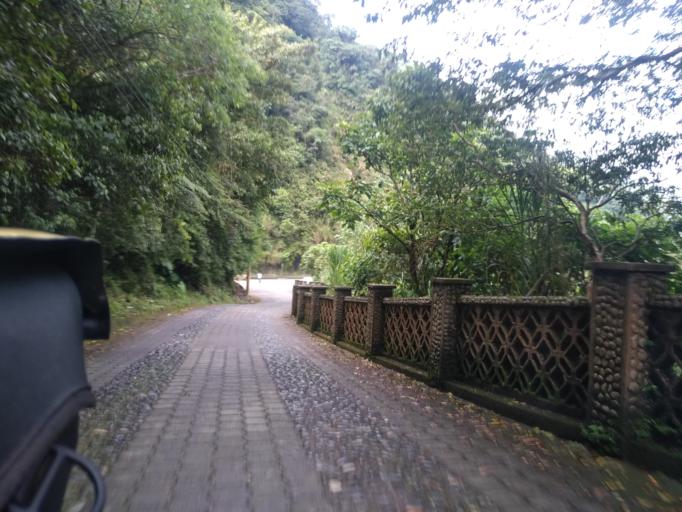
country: EC
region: Tungurahua
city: Banos
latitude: -1.4001
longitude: -78.2938
